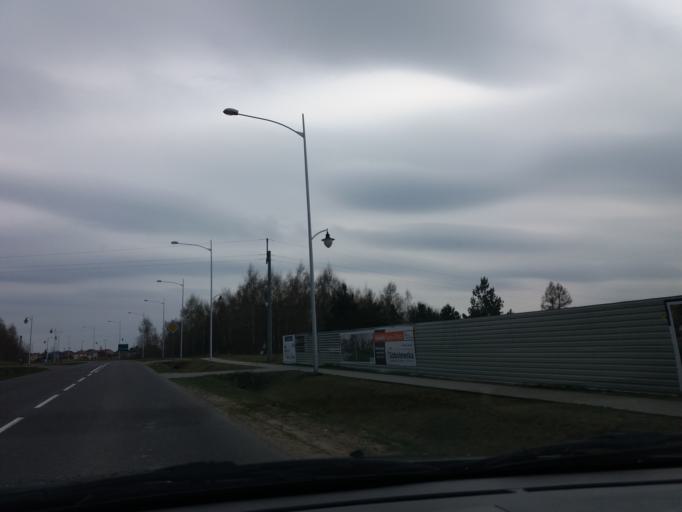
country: PL
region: Masovian Voivodeship
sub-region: Powiat mlawski
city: Mlawa
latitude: 53.1310
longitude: 20.3636
